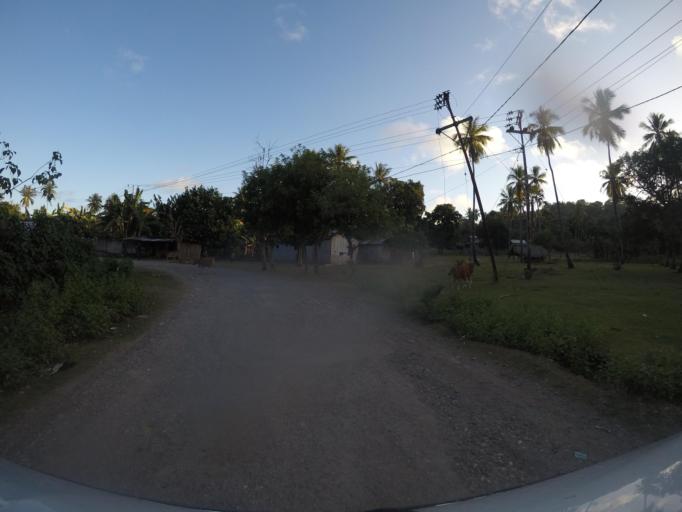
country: TL
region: Baucau
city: Venilale
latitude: -8.7415
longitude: 126.7135
